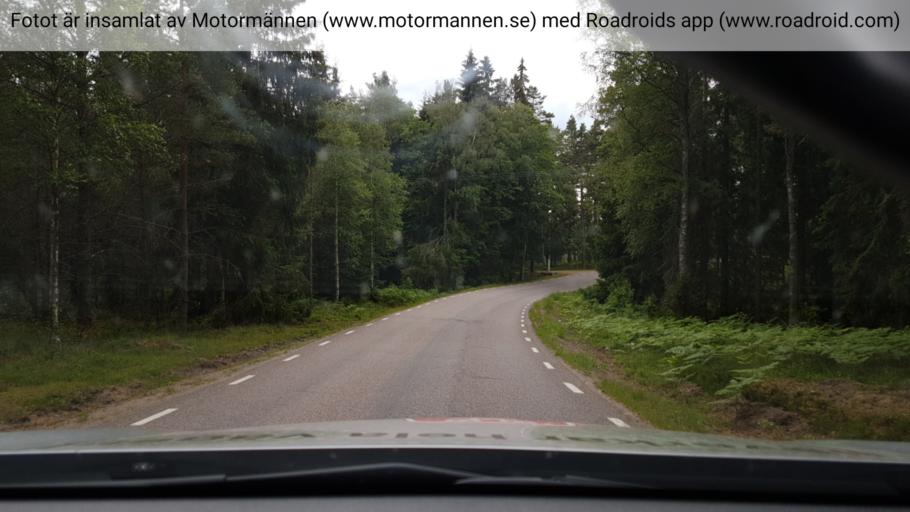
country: SE
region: Joenkoeping
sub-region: Habo Kommun
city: Habo
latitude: 58.0256
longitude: 14.0152
